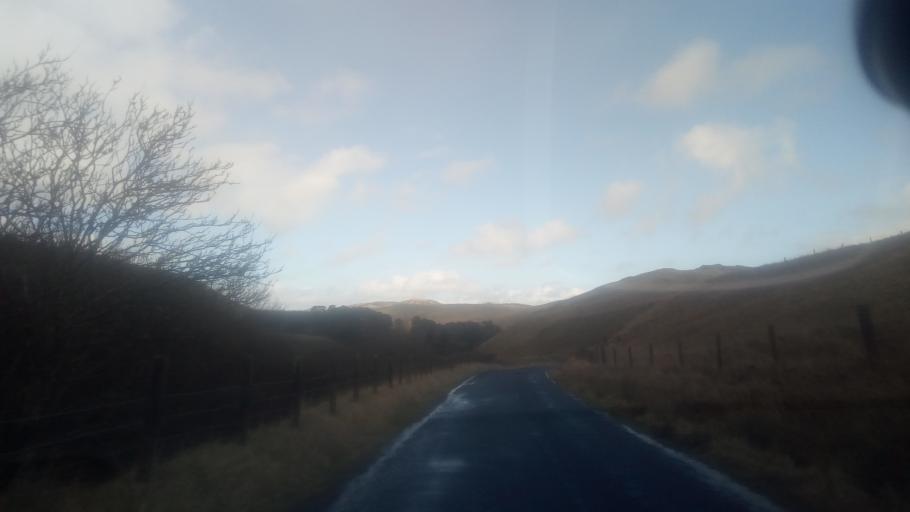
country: GB
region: Scotland
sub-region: The Scottish Borders
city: Innerleithen
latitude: 55.4548
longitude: -3.1063
